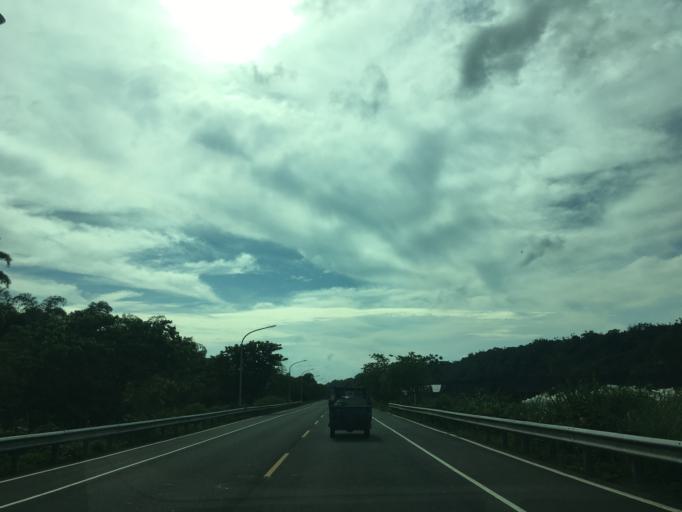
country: TW
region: Taiwan
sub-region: Chiayi
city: Jiayi Shi
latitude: 23.4486
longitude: 120.5760
